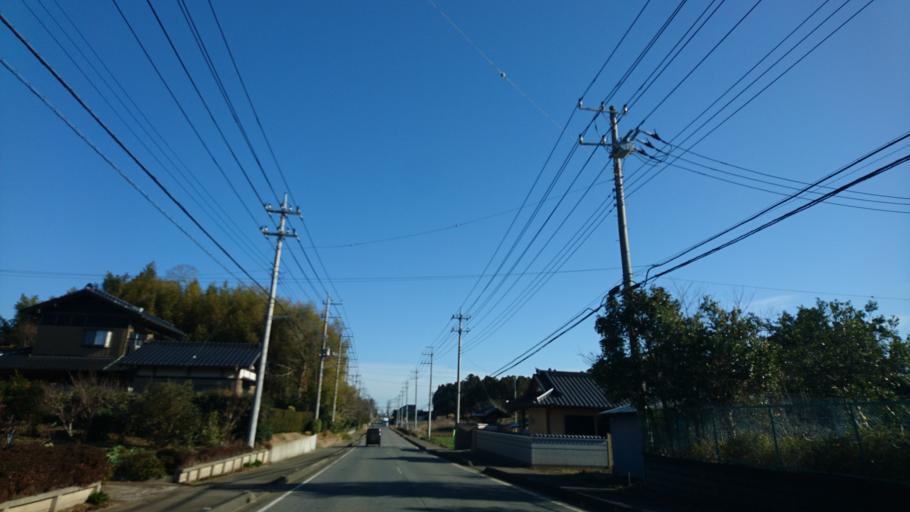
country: JP
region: Chiba
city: Oami
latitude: 35.5819
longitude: 140.3086
